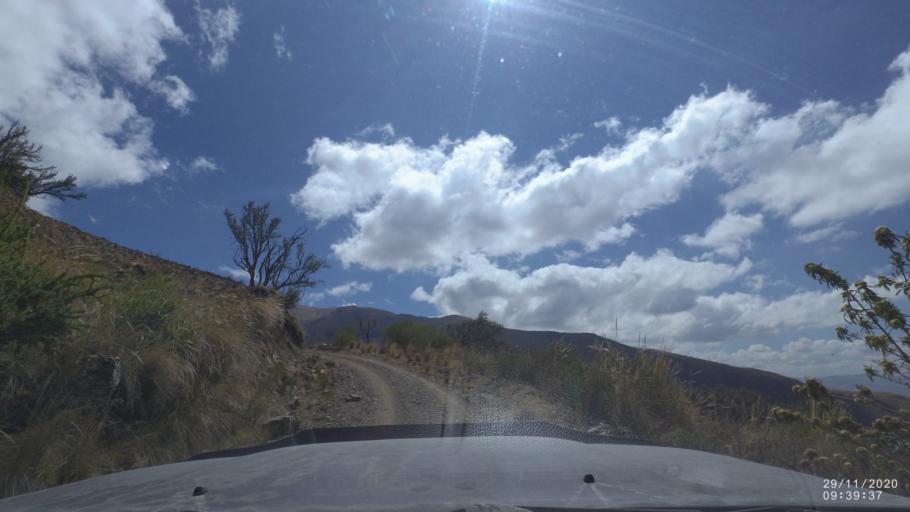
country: BO
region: Cochabamba
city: Cochabamba
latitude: -17.3046
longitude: -66.1824
